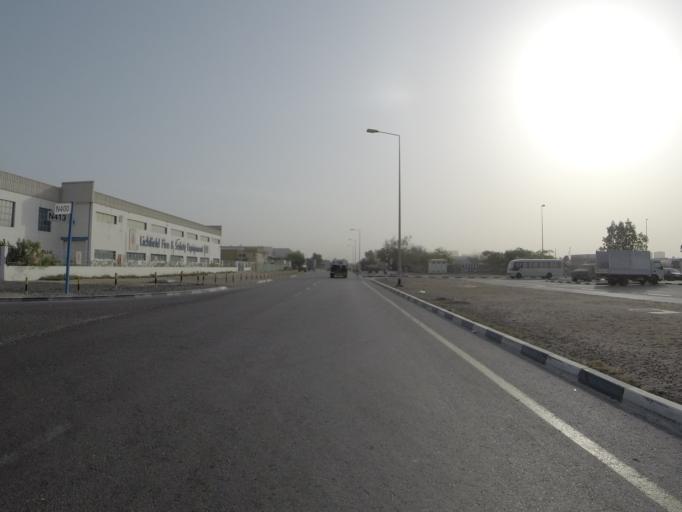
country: AE
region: Dubai
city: Dubai
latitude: 24.9672
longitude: 55.0682
